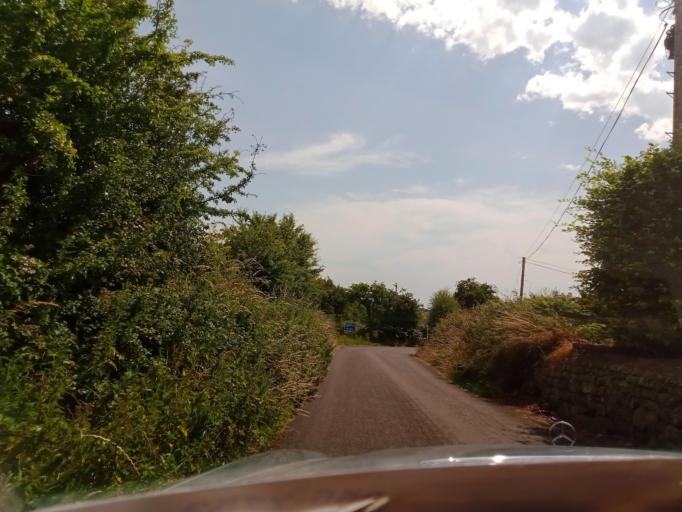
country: IE
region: Leinster
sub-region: Kilkenny
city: Mooncoin
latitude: 52.2701
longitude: -7.2133
